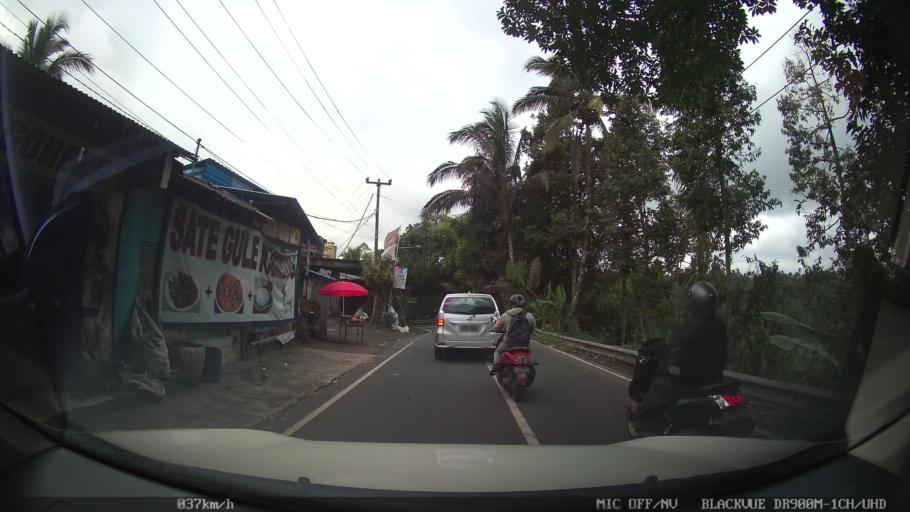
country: ID
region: Bali
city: Petang
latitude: -8.3709
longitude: 115.2244
